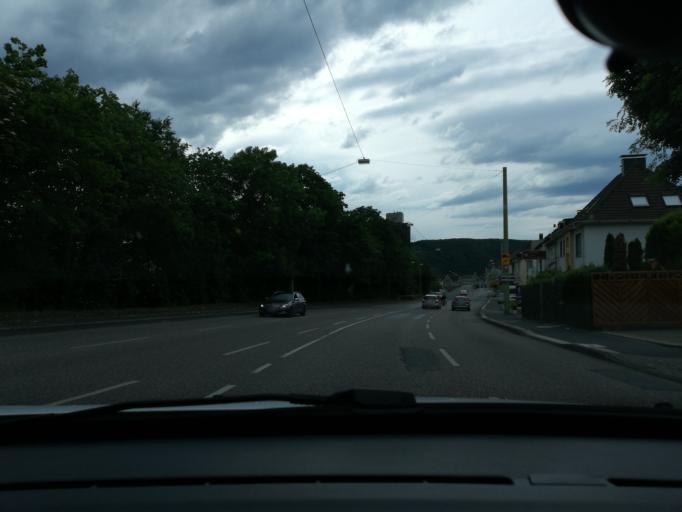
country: DE
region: North Rhine-Westphalia
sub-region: Regierungsbezirk Arnsberg
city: Hagen
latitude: 51.3627
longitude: 7.4711
